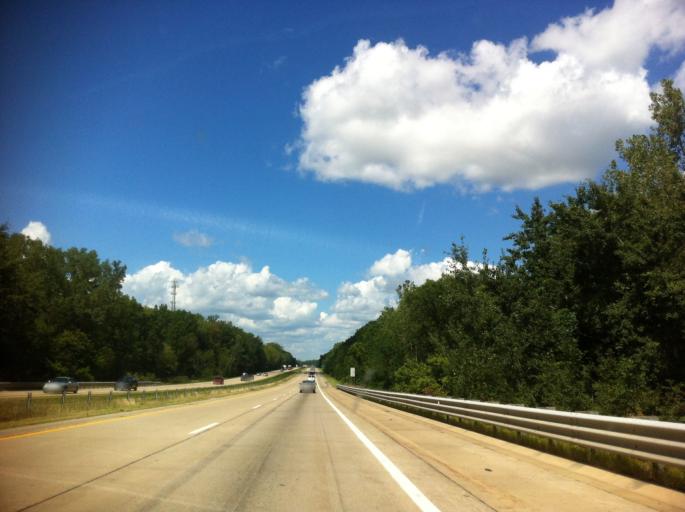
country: US
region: Michigan
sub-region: Monroe County
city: Dundee
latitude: 41.9162
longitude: -83.6619
